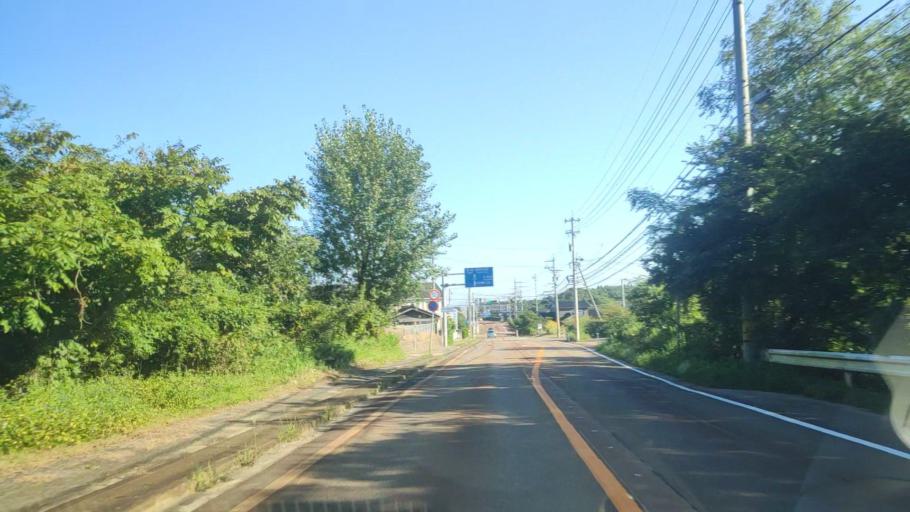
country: JP
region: Ishikawa
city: Hakui
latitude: 36.8679
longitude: 136.7723
